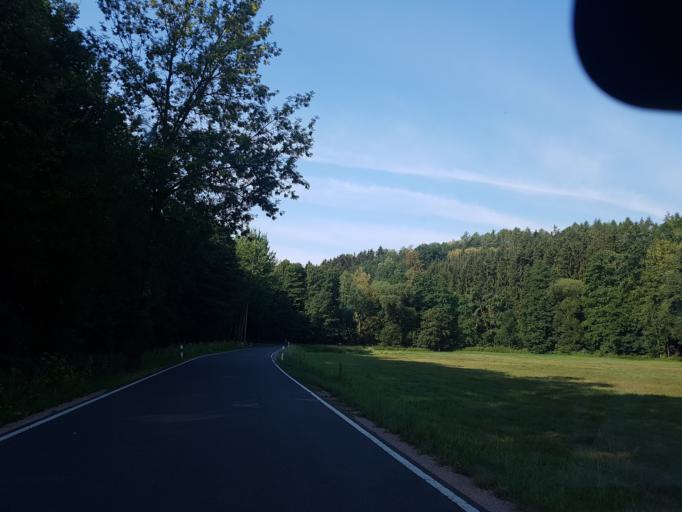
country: DE
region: Saxony
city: Waldheim
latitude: 51.0778
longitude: 13.0462
